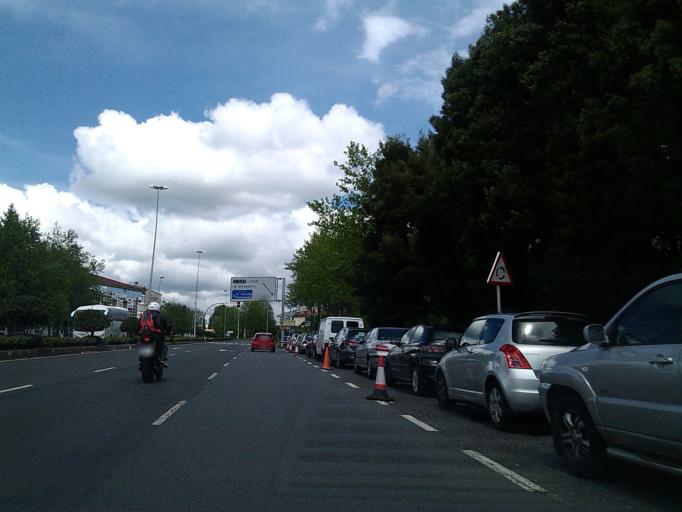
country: ES
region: Galicia
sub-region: Provincia da Coruna
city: Santiago de Compostela
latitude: 42.8881
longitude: -8.5324
